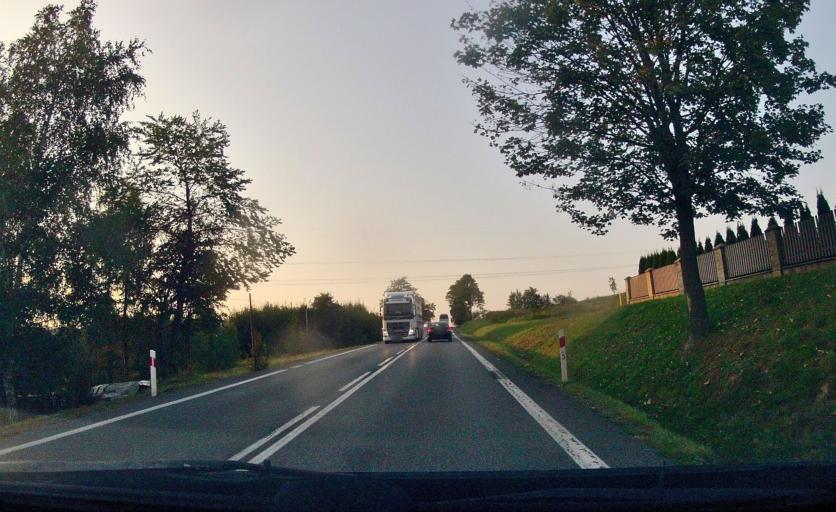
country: PL
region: Subcarpathian Voivodeship
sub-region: Powiat debicki
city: Slotowa
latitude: 49.9177
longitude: 21.3437
